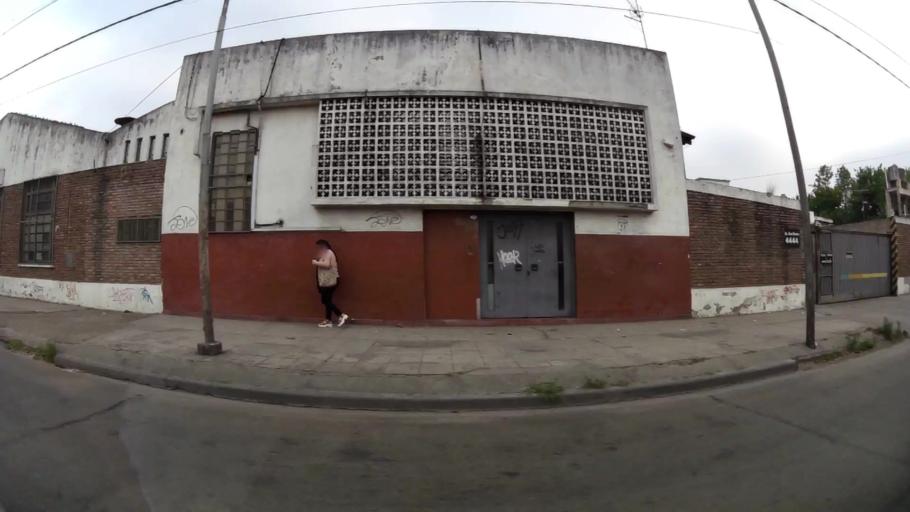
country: AR
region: Buenos Aires
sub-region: Partido de Moron
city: Moron
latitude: -34.6707
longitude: -58.6055
